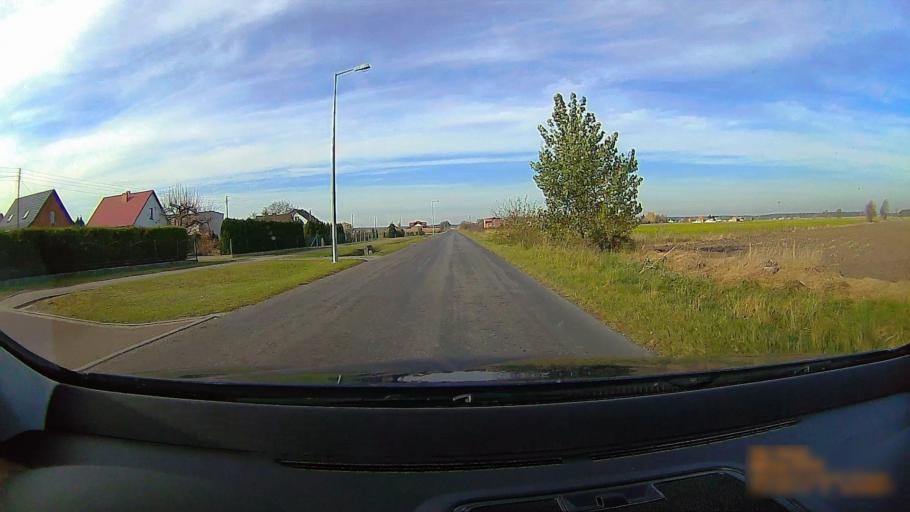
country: PL
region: Greater Poland Voivodeship
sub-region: Powiat ostrzeszowski
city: Doruchow
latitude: 51.4216
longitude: 18.0633
